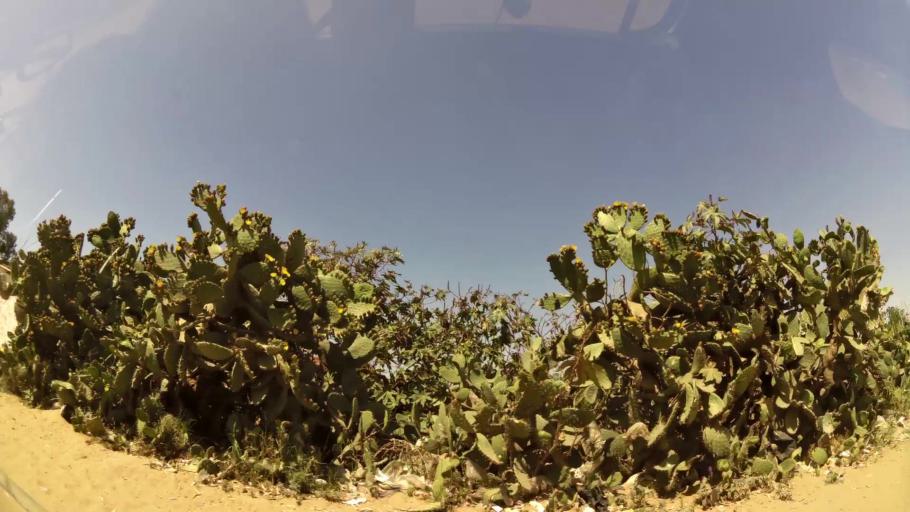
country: MA
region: Gharb-Chrarda-Beni Hssen
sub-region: Kenitra Province
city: Kenitra
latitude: 34.2300
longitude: -6.5364
